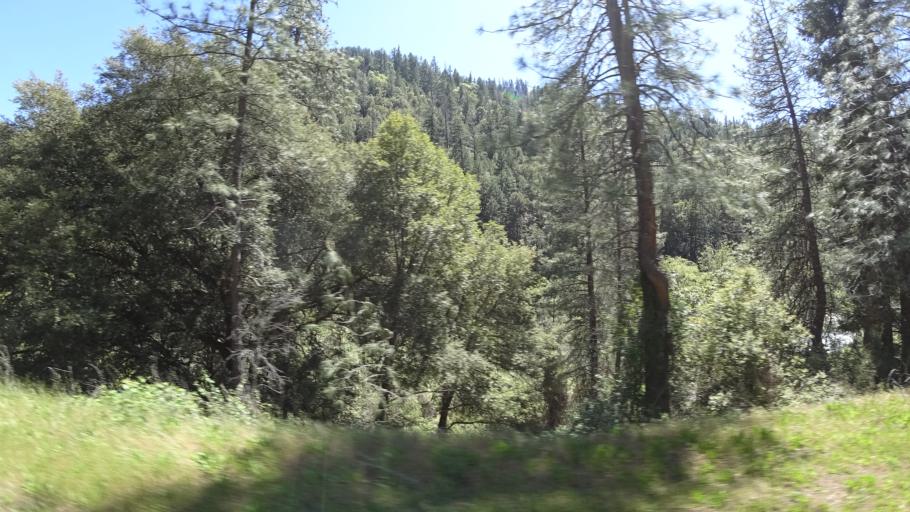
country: US
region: California
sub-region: Humboldt County
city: Willow Creek
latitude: 40.7981
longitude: -123.3989
